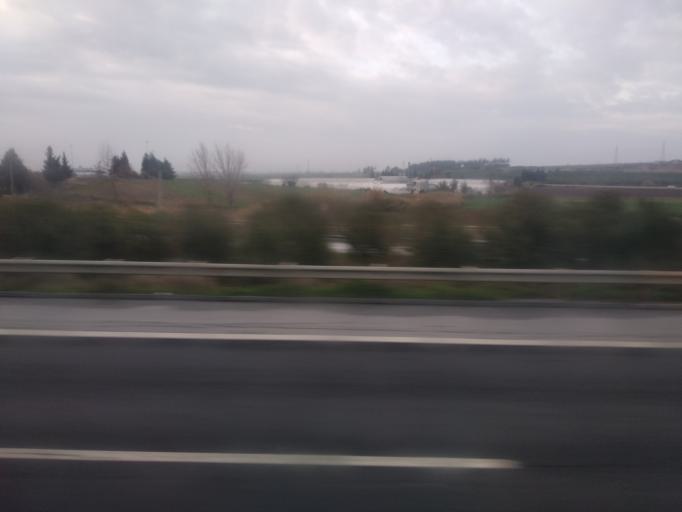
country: TR
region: Mersin
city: Yenice
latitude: 37.0383
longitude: 35.1702
